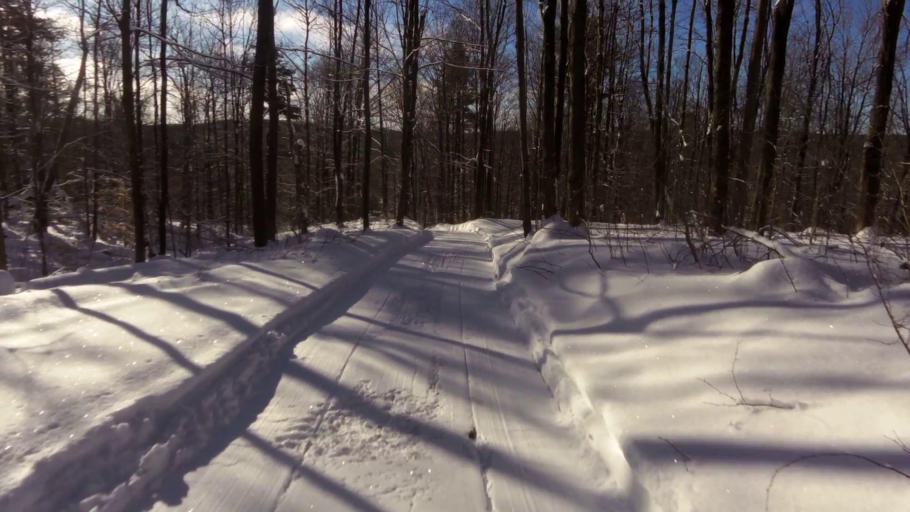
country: US
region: New York
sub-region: Chautauqua County
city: Falconer
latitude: 42.2584
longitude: -79.1717
